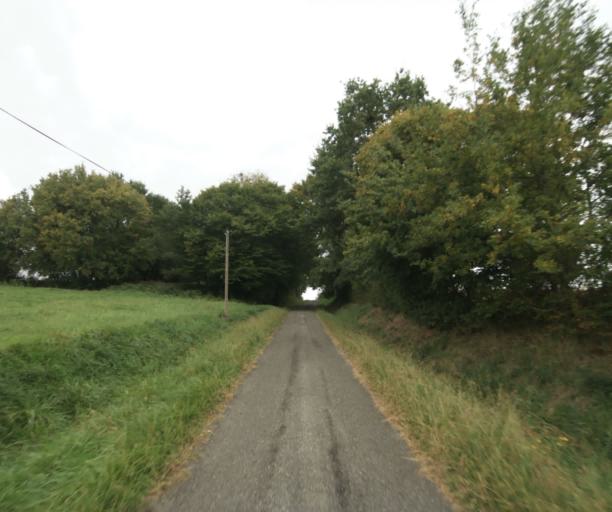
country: FR
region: Midi-Pyrenees
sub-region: Departement du Gers
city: Eauze
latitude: 43.8981
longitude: 0.0541
